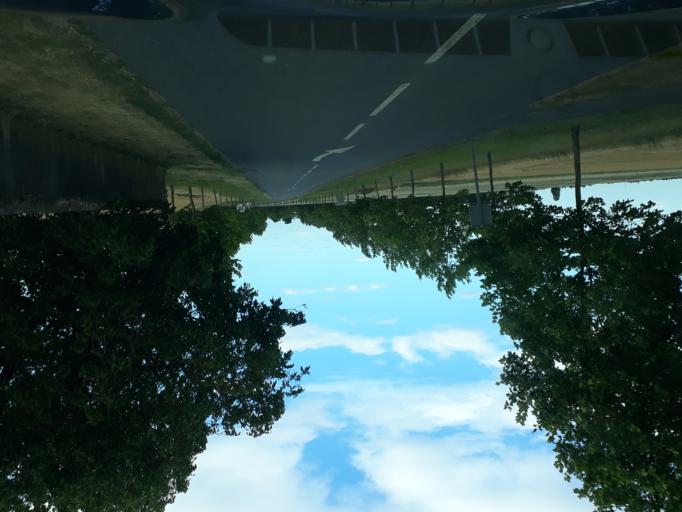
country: FR
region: Centre
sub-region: Departement du Loir-et-Cher
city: Mer
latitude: 47.8019
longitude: 1.5168
